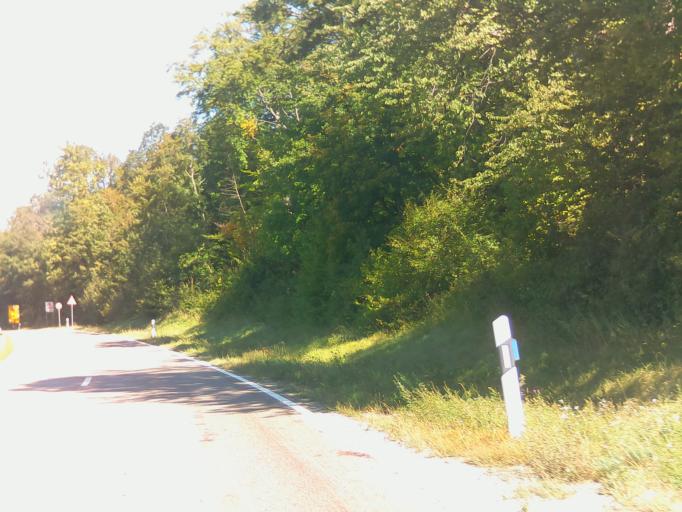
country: DE
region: Baden-Wuerttemberg
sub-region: Karlsruhe Region
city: Birkenfeld
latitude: 48.8916
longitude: 8.6367
